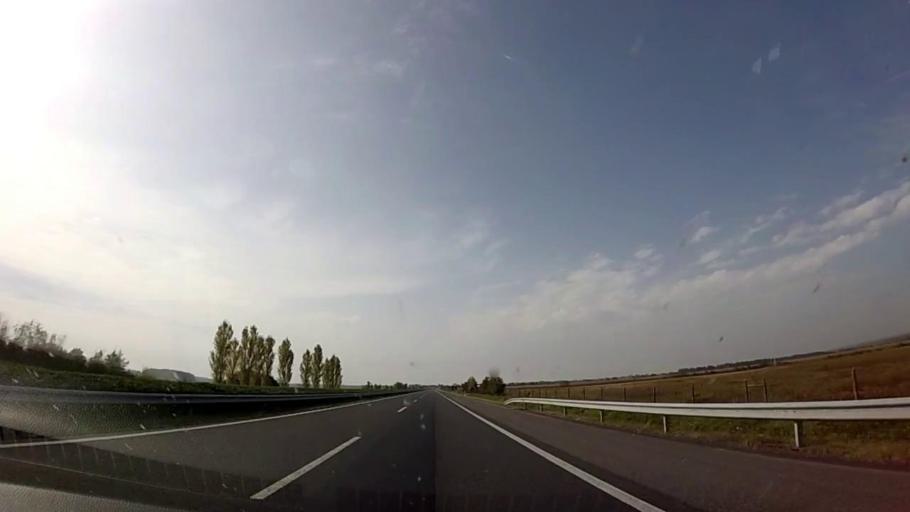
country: HU
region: Zala
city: Becsehely
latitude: 46.4282
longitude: 16.7846
